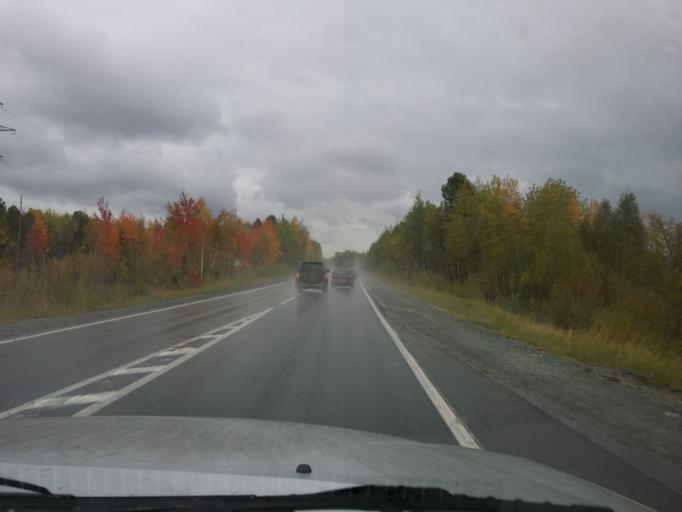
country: RU
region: Khanty-Mansiyskiy Avtonomnyy Okrug
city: Megion
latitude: 61.1297
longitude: 75.7838
